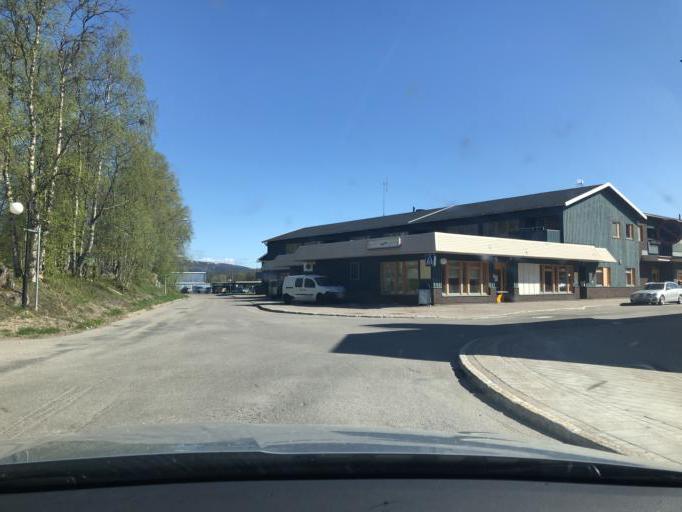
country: SE
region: Norrbotten
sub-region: Arjeplogs Kommun
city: Arjeplog
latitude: 66.0518
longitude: 17.8882
